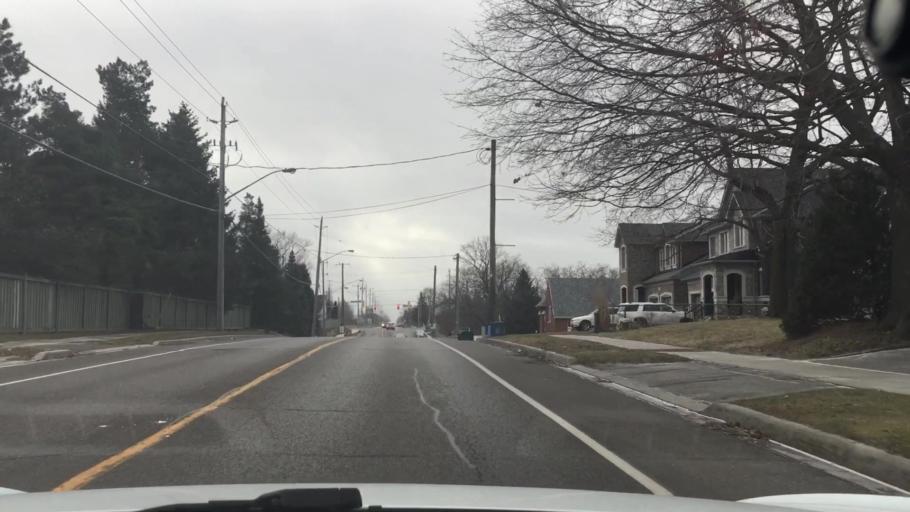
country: CA
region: Ontario
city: Oshawa
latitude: 43.9128
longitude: -78.7893
